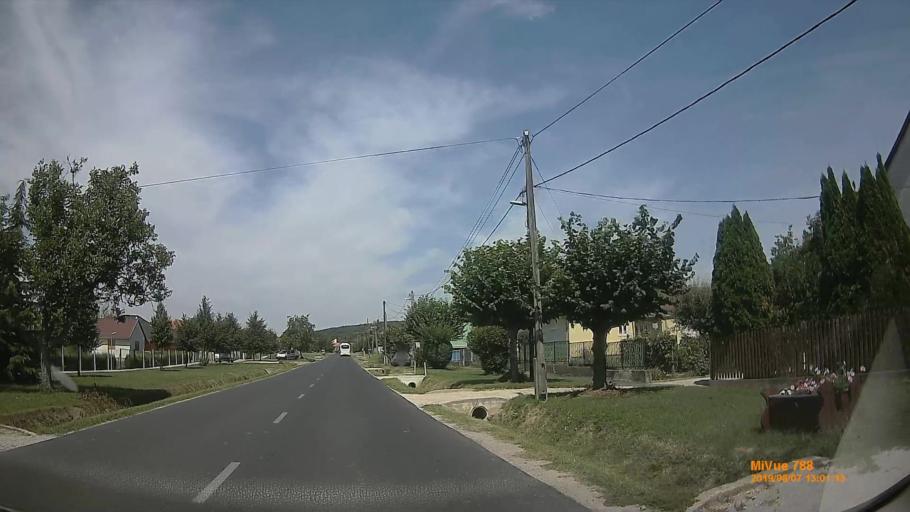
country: HU
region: Zala
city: Cserszegtomaj
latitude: 46.8022
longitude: 17.2322
